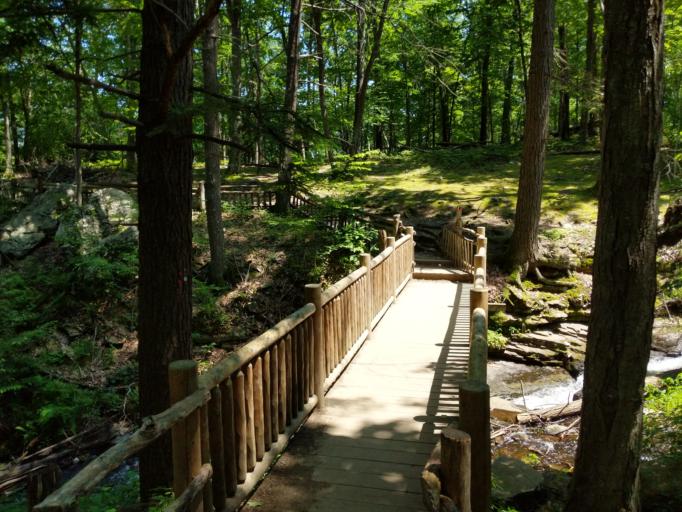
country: US
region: Pennsylvania
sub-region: Pike County
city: Saw Creek
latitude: 41.1203
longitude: -75.0165
